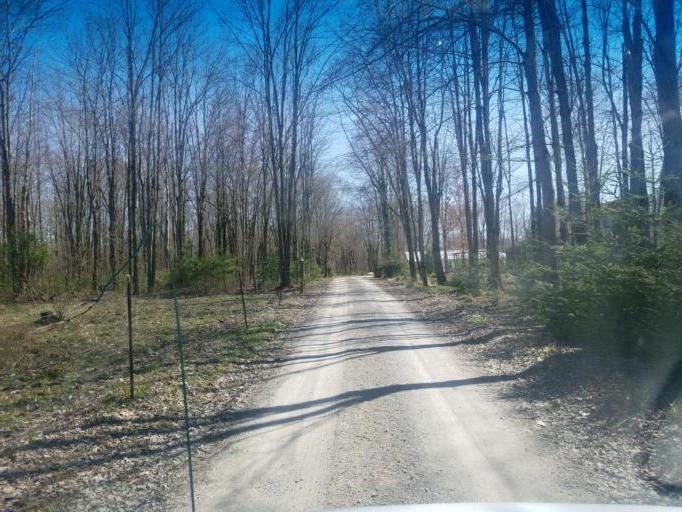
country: US
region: Ohio
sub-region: Knox County
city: Oak Hill
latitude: 40.3319
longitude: -82.2419
